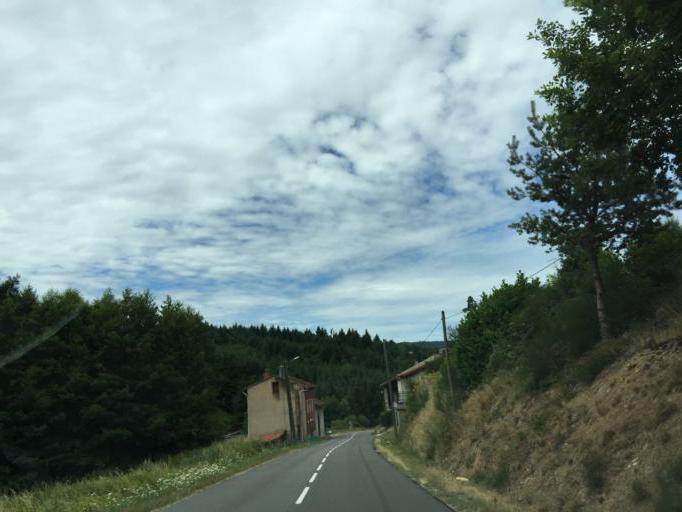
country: FR
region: Rhone-Alpes
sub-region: Departement de la Loire
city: Perigneux
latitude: 45.4068
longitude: 4.1208
